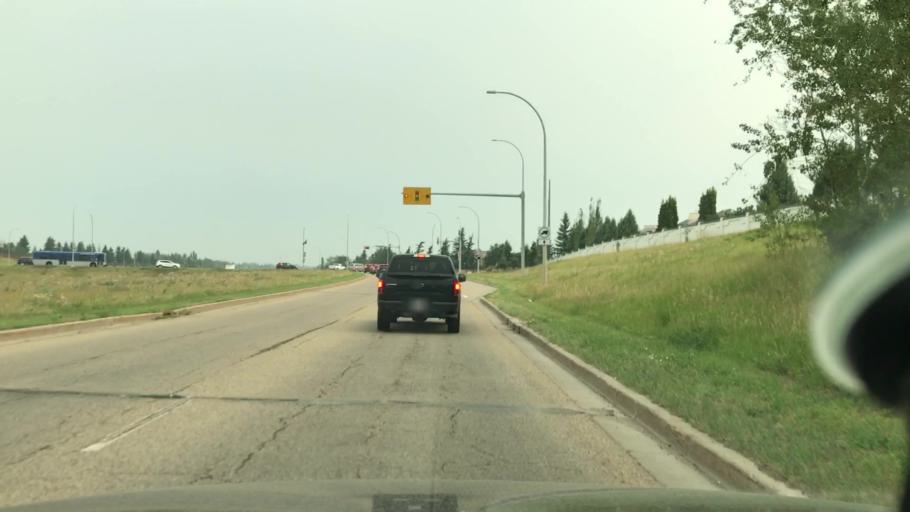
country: CA
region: Alberta
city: Edmonton
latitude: 53.4669
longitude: -113.5821
